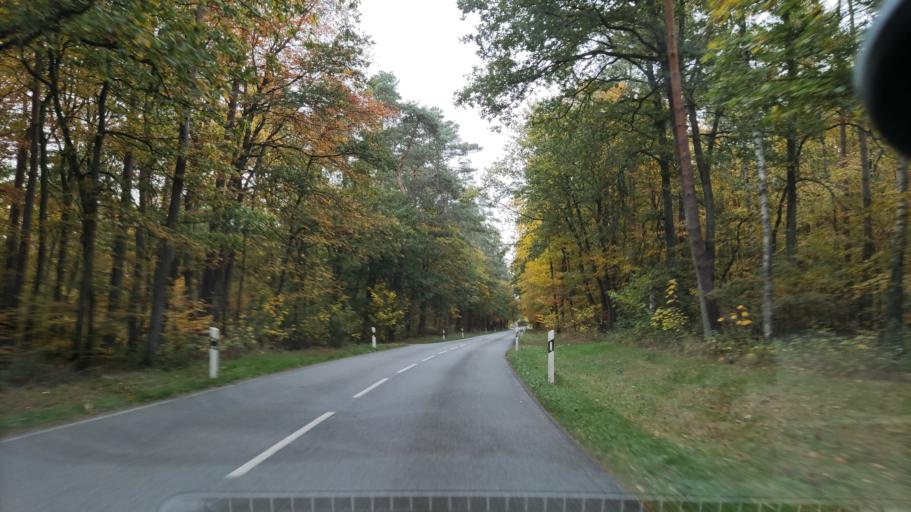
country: DE
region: Mecklenburg-Vorpommern
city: Boizenburg
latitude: 53.3808
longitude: 10.8525
